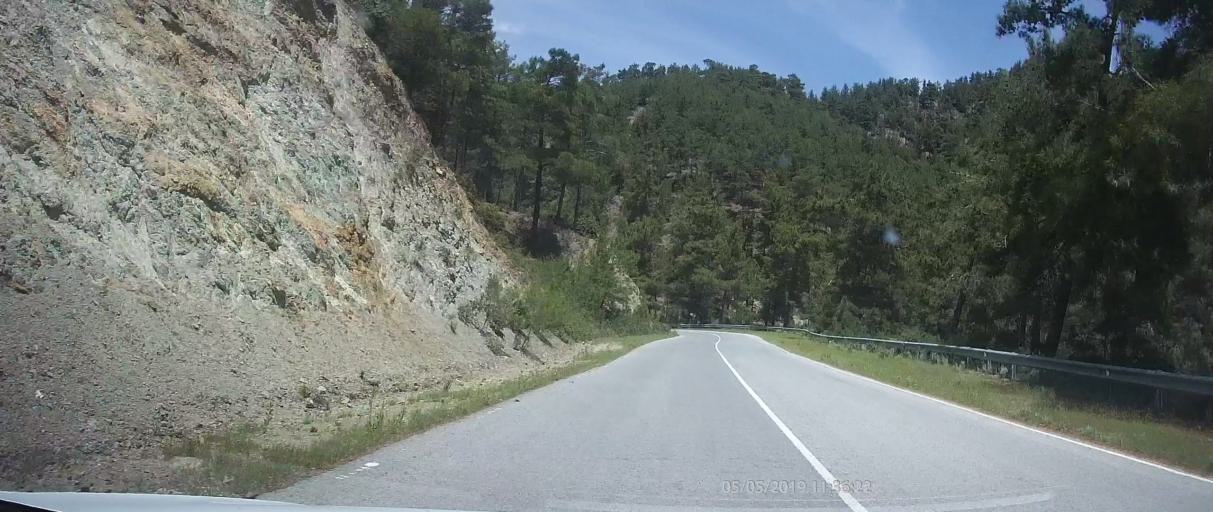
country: CY
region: Lefkosia
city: Kato Pyrgos
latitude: 34.9728
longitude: 32.6524
